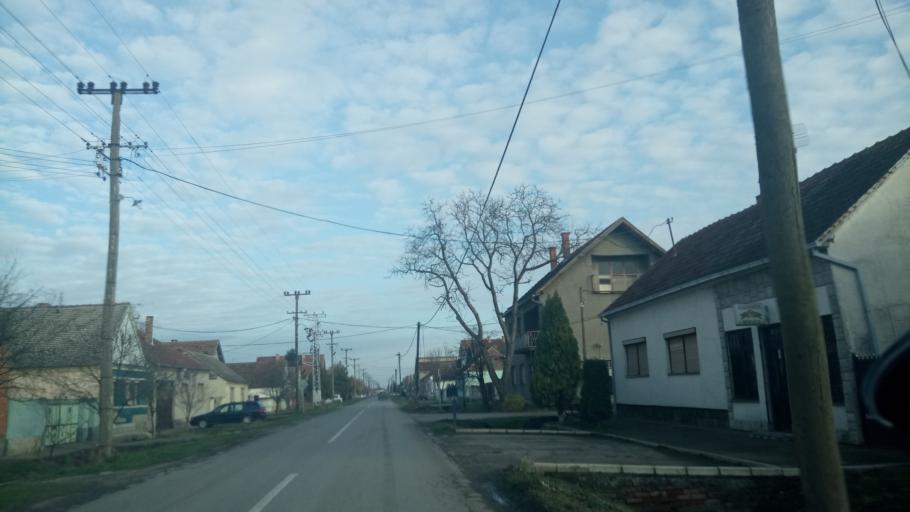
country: RS
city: Vojka
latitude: 44.9354
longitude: 20.1552
